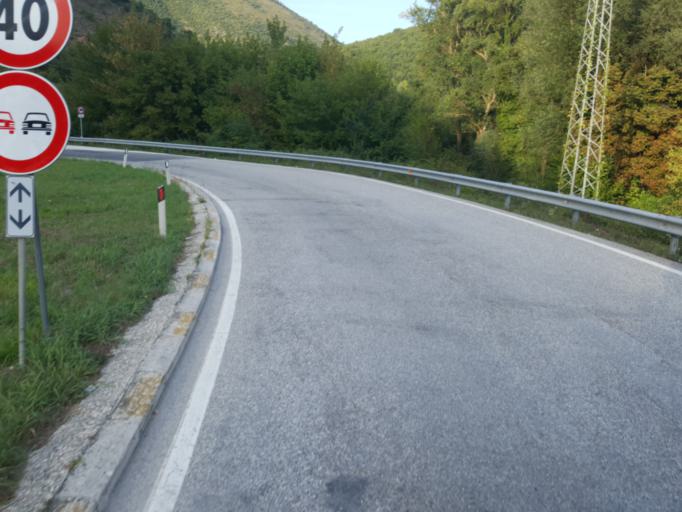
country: IT
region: The Marches
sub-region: Provincia di Ancona
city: Fabriano
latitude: 43.3125
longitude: 12.8598
